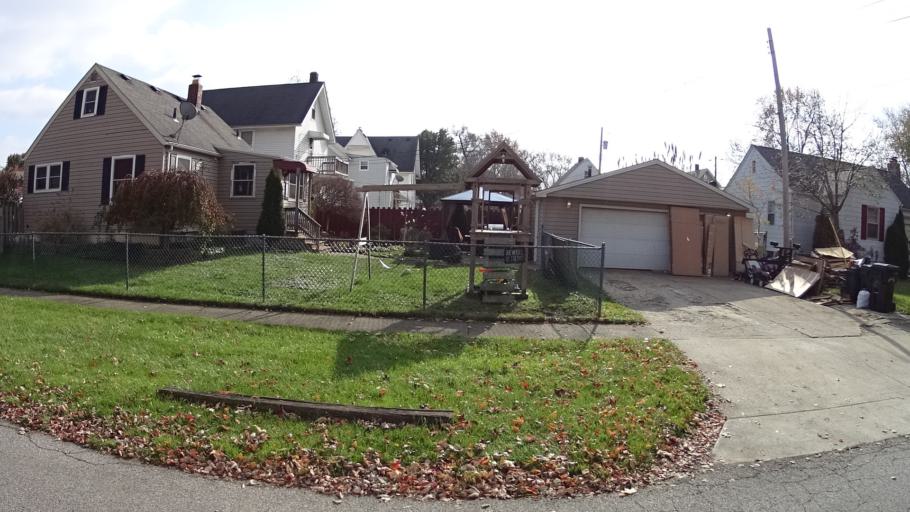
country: US
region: Ohio
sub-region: Lorain County
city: Elyria
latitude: 41.3769
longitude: -82.0907
